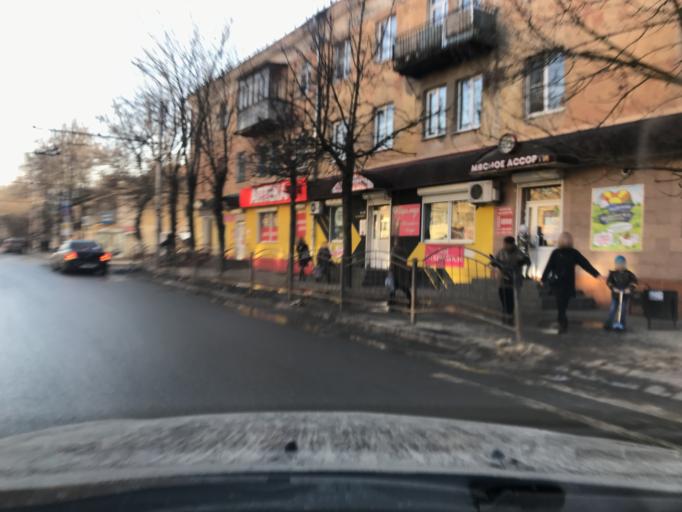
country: RU
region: Kaluga
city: Kaluga
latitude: 54.5318
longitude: 36.2613
